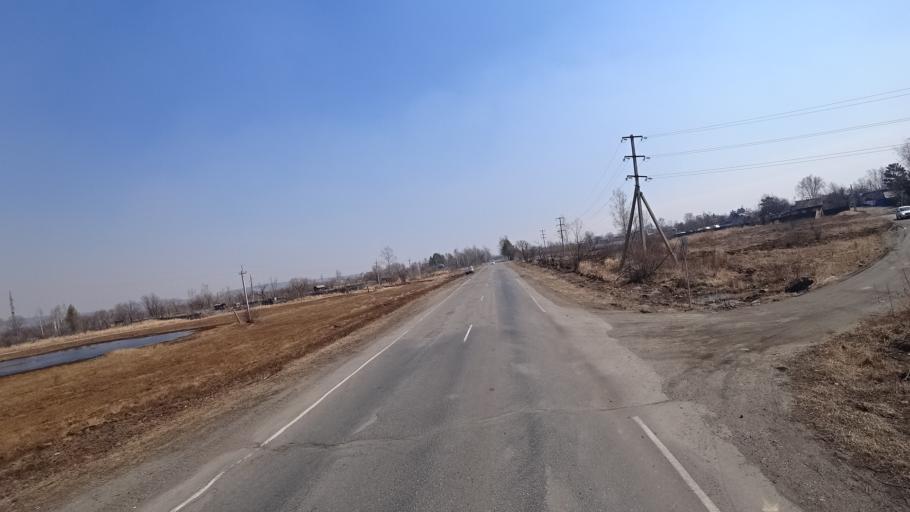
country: RU
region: Amur
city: Novobureyskiy
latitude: 49.7899
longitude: 129.8402
